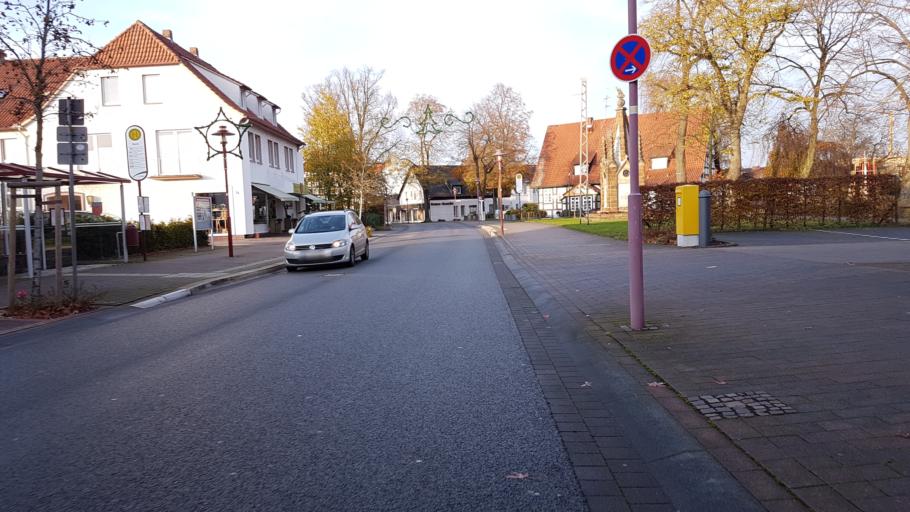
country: DE
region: North Rhine-Westphalia
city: Rahden
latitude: 52.4308
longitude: 8.6177
